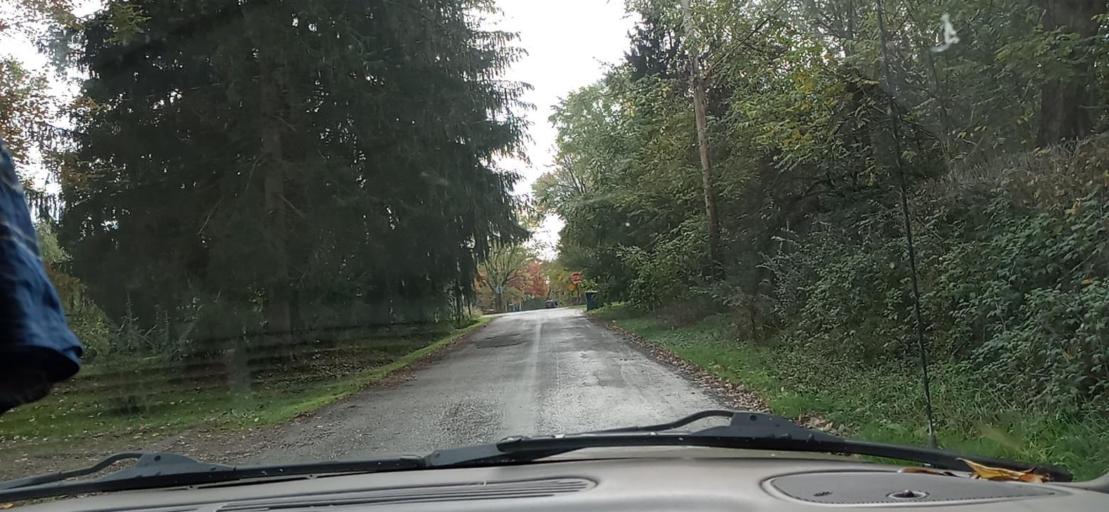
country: US
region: Ohio
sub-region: Summit County
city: Portage Lakes
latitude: 41.0127
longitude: -81.4897
